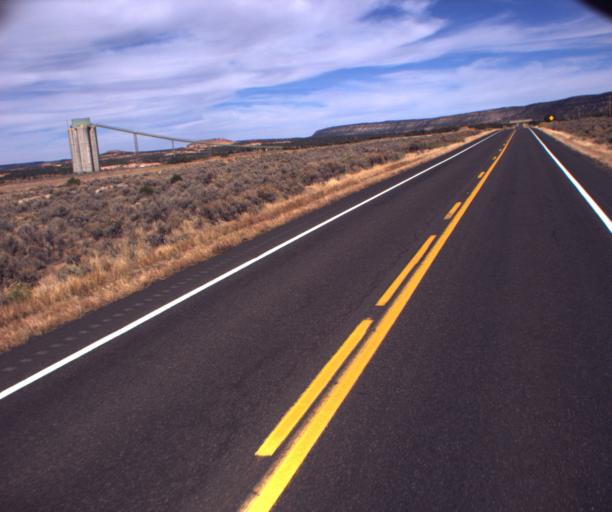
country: US
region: Arizona
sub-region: Navajo County
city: Kayenta
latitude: 36.5513
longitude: -110.5251
